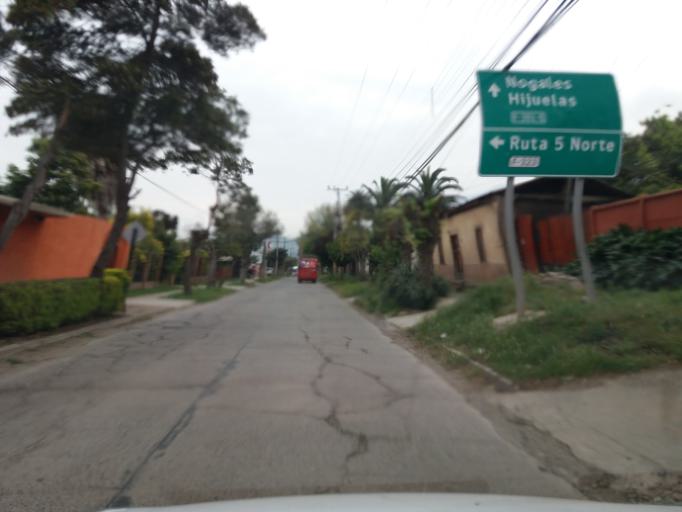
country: CL
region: Valparaiso
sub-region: Provincia de Quillota
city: Hacienda La Calera
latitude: -32.8078
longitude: -71.1420
